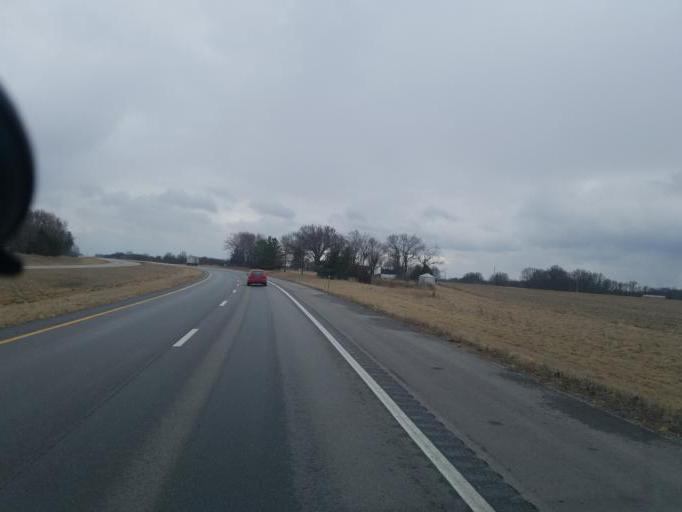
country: US
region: Missouri
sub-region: Randolph County
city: Moberly
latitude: 39.3782
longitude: -92.4137
